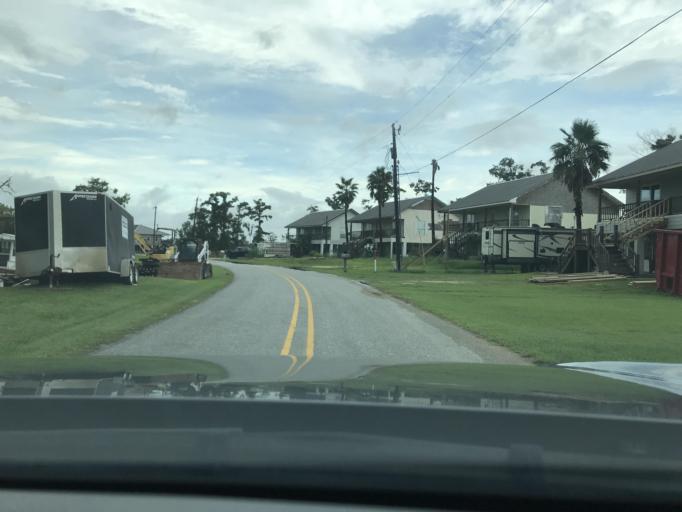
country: US
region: Louisiana
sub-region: Calcasieu Parish
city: Moss Bluff
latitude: 30.2745
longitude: -93.2211
